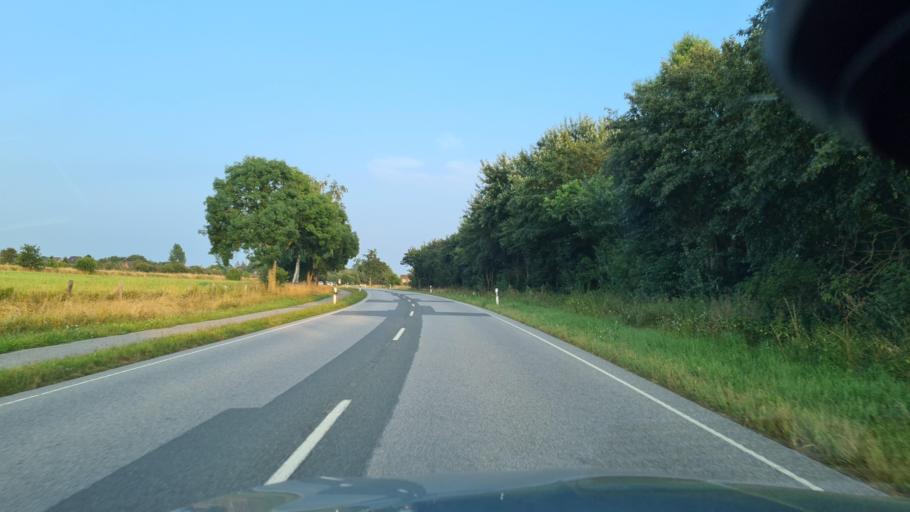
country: DE
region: Schleswig-Holstein
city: Schobull
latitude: 54.4987
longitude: 9.0204
